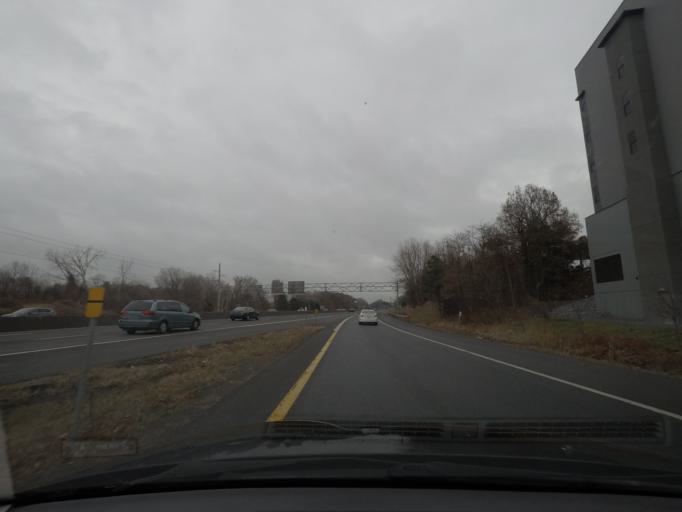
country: US
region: New York
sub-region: Albany County
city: Roessleville
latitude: 42.6915
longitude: -73.8222
